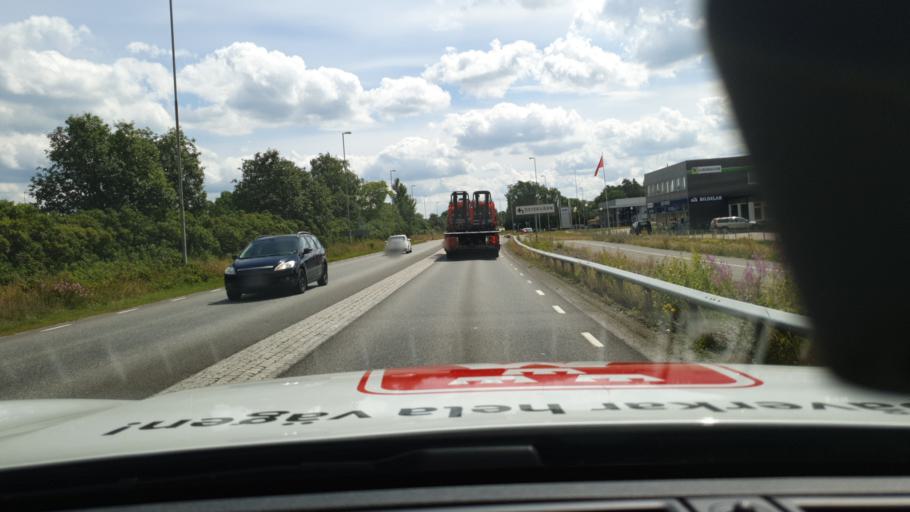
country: SE
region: Skane
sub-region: Hassleholms Kommun
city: Hassleholm
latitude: 56.1490
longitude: 13.7846
